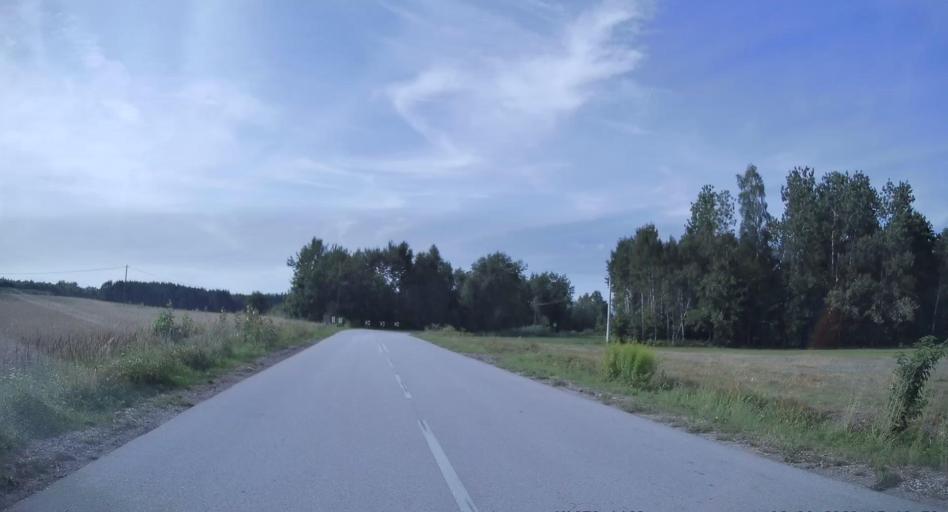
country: PL
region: Lodz Voivodeship
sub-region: Powiat opoczynski
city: Mniszkow
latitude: 51.3543
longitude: 20.0377
